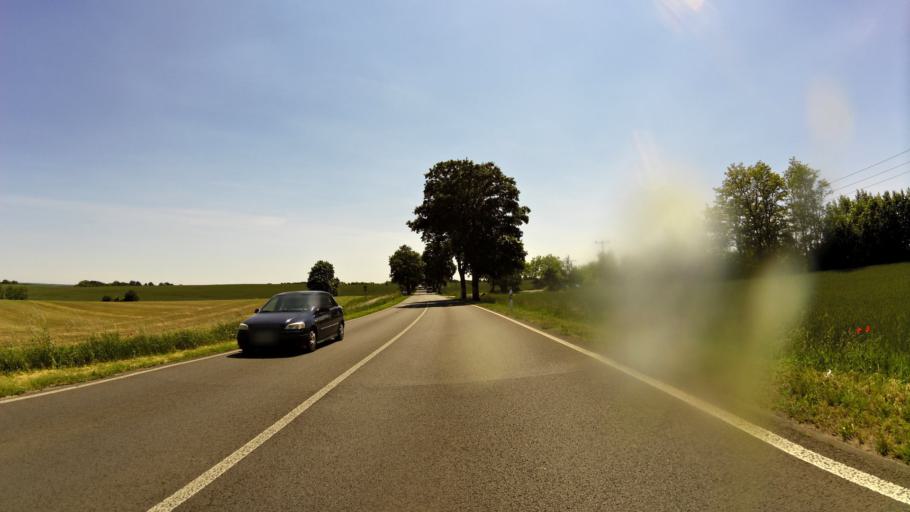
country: DE
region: Brandenburg
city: Lebus
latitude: 52.4000
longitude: 14.5169
